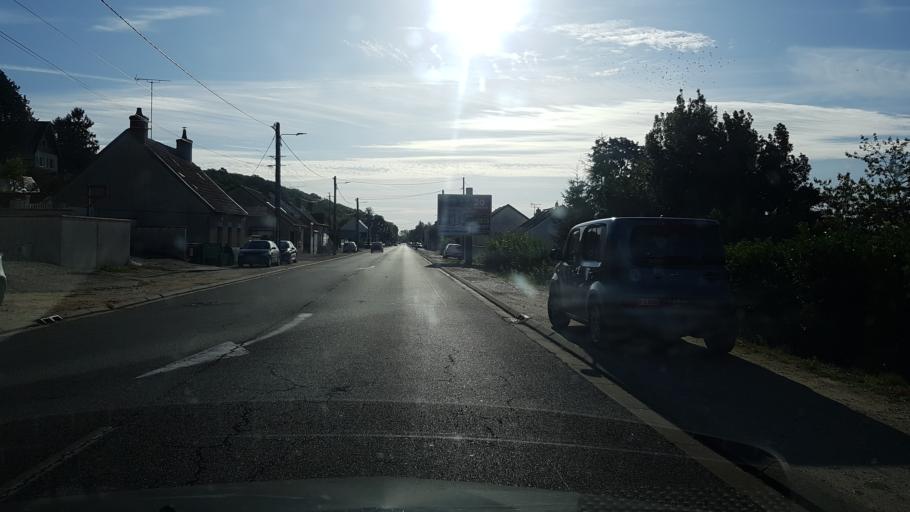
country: FR
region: Centre
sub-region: Departement du Loiret
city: Saint-Martin-sur-Ocre
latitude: 47.6769
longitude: 2.6511
